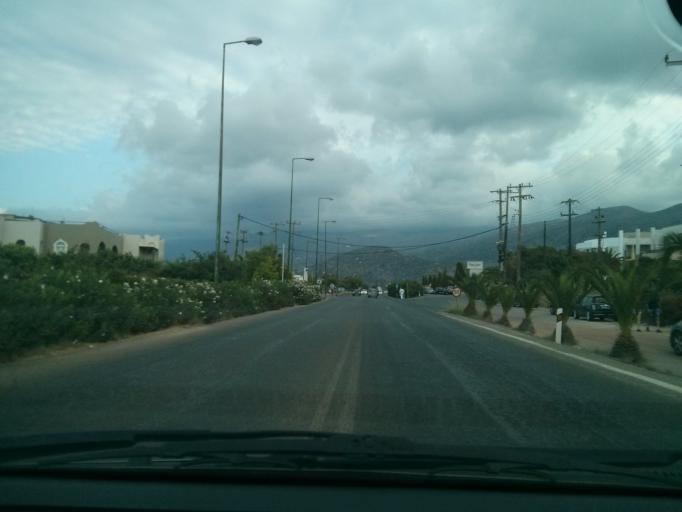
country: GR
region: Crete
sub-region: Nomos Irakleiou
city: Stalis
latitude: 35.3029
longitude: 25.4189
